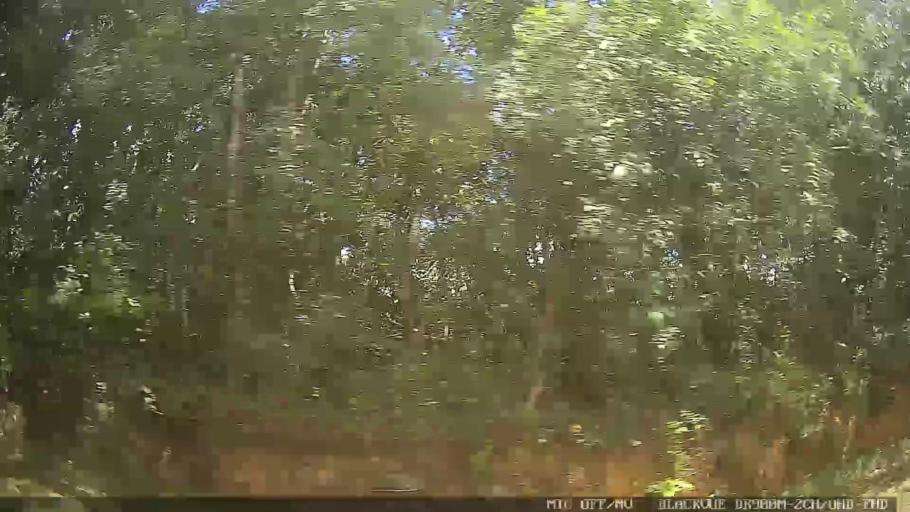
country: BR
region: Minas Gerais
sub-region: Extrema
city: Extrema
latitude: -22.7423
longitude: -46.4311
